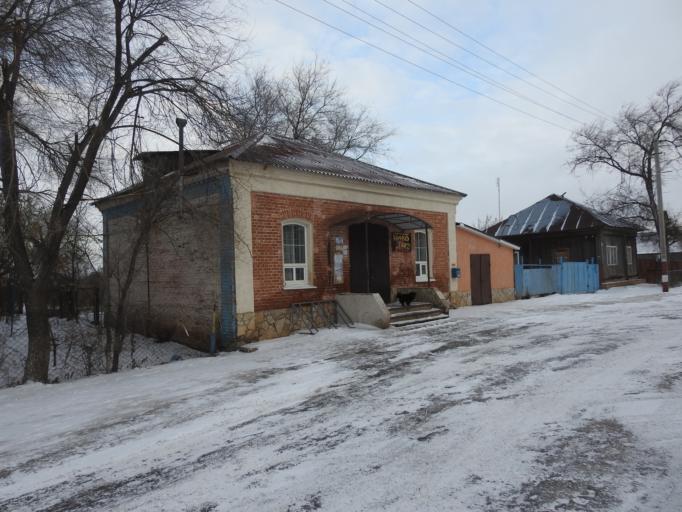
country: RU
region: Saratov
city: Krasnyy Yar
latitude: 51.5649
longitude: 46.5034
